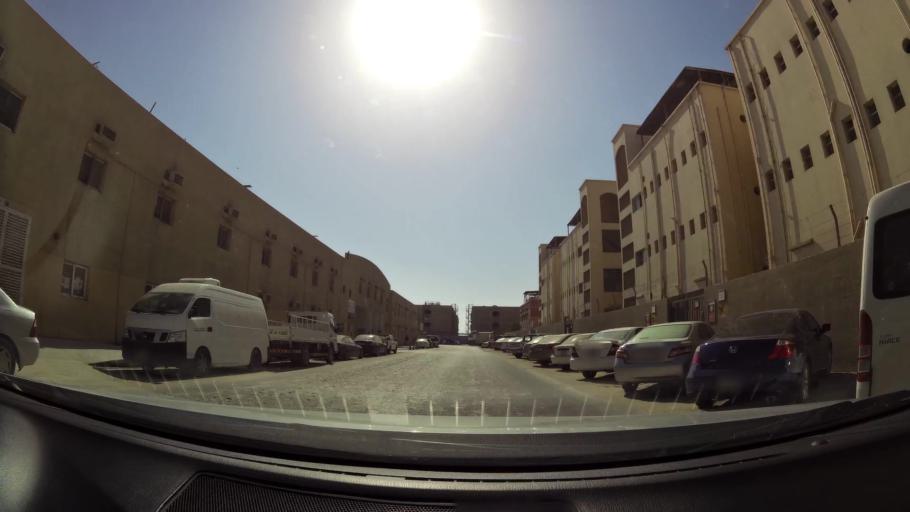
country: AE
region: Dubai
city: Dubai
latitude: 25.0107
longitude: 55.1049
